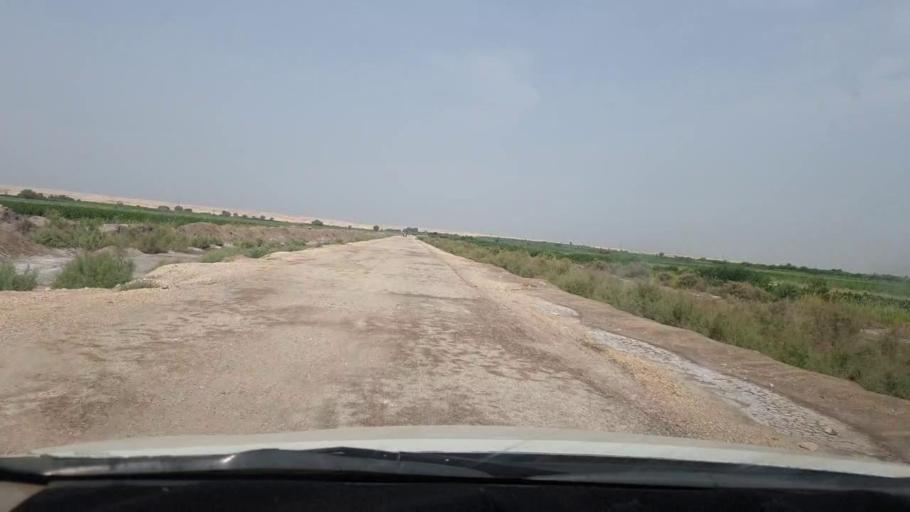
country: PK
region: Sindh
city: Rohri
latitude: 27.5949
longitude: 68.9989
